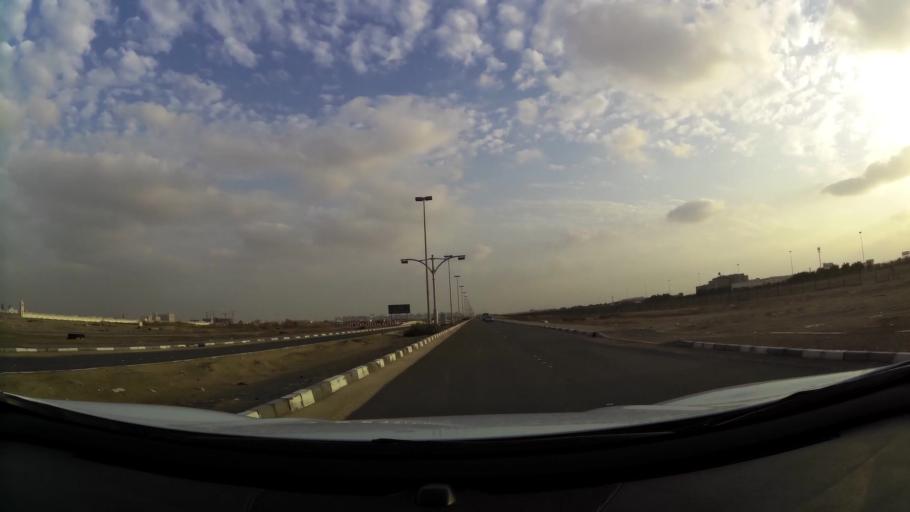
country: AE
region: Abu Dhabi
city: Abu Dhabi
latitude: 24.3686
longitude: 54.5278
